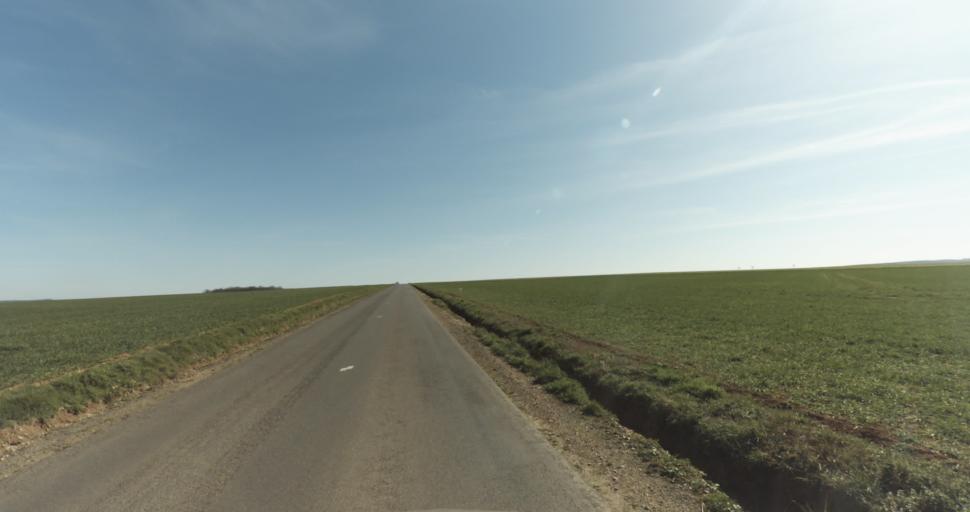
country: FR
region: Lower Normandy
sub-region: Departement du Calvados
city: Saint-Pierre-sur-Dives
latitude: 48.9990
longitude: -0.0474
